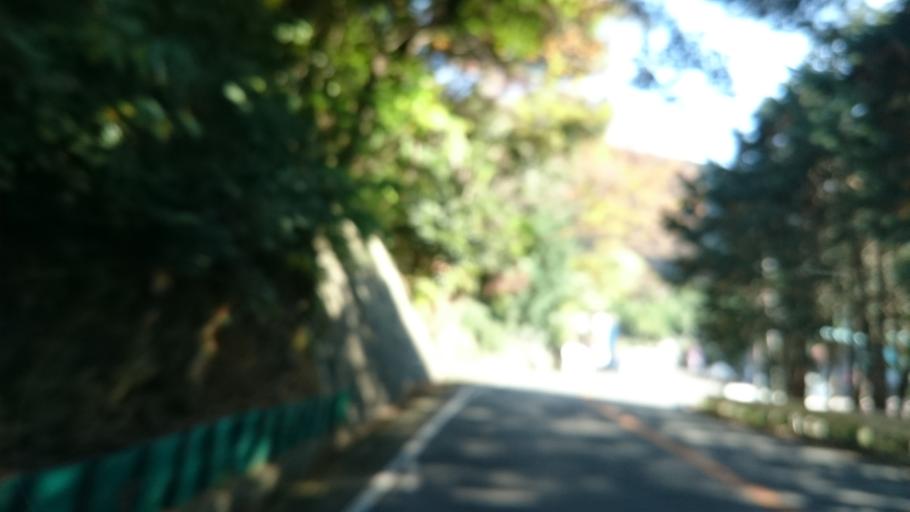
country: JP
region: Shizuoka
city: Heda
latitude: 34.9663
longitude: 138.8146
